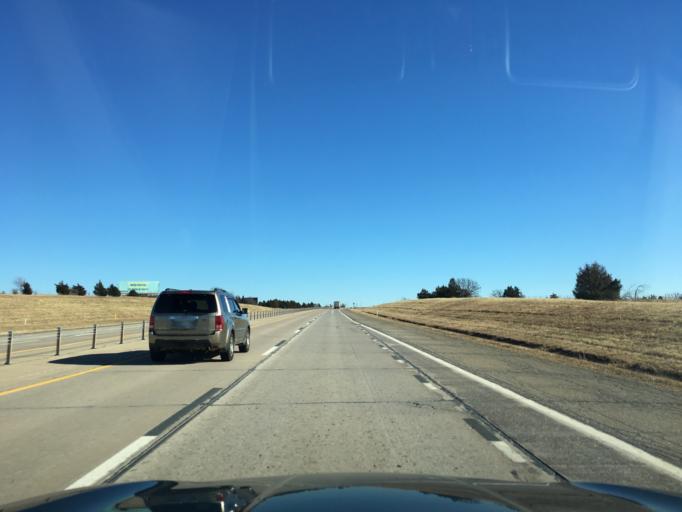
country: US
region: Oklahoma
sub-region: Pawnee County
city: Pawnee
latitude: 36.2395
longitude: -96.9376
